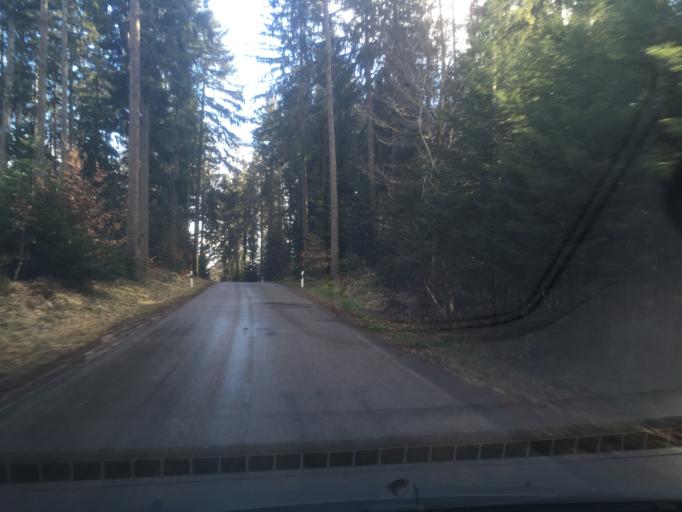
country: DE
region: Baden-Wuerttemberg
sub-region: Freiburg Region
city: Hochenschwand
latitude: 47.6849
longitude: 8.1471
